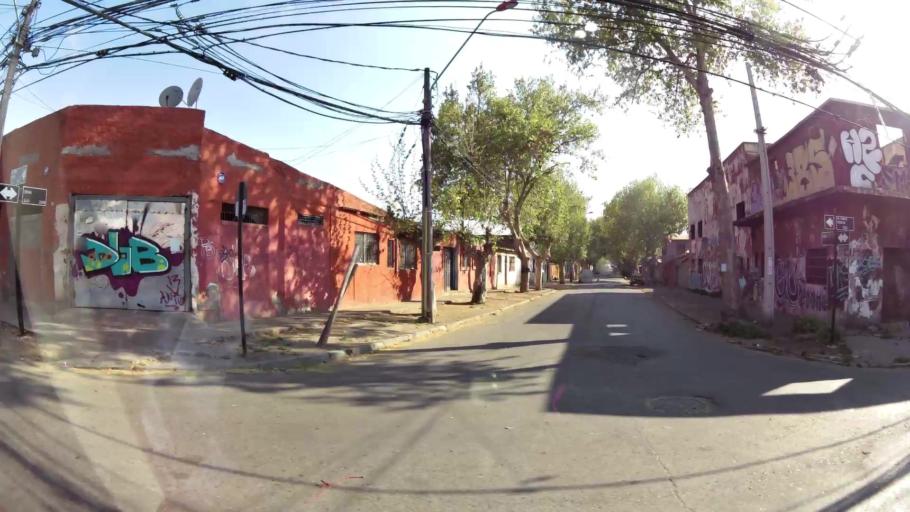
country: CL
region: Santiago Metropolitan
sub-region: Provincia de Santiago
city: Santiago
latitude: -33.3976
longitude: -70.6736
